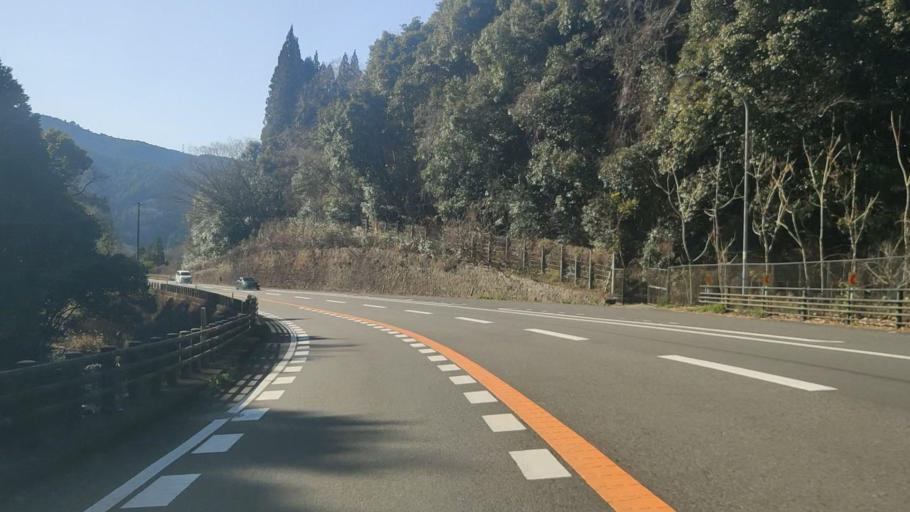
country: JP
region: Oita
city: Tsukumiura
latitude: 32.9984
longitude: 131.7674
